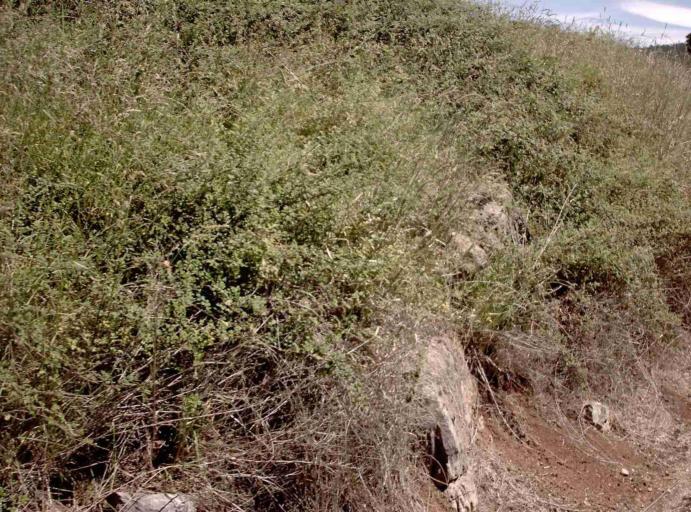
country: AU
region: Victoria
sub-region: East Gippsland
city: Lakes Entrance
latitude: -37.3941
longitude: 148.2173
